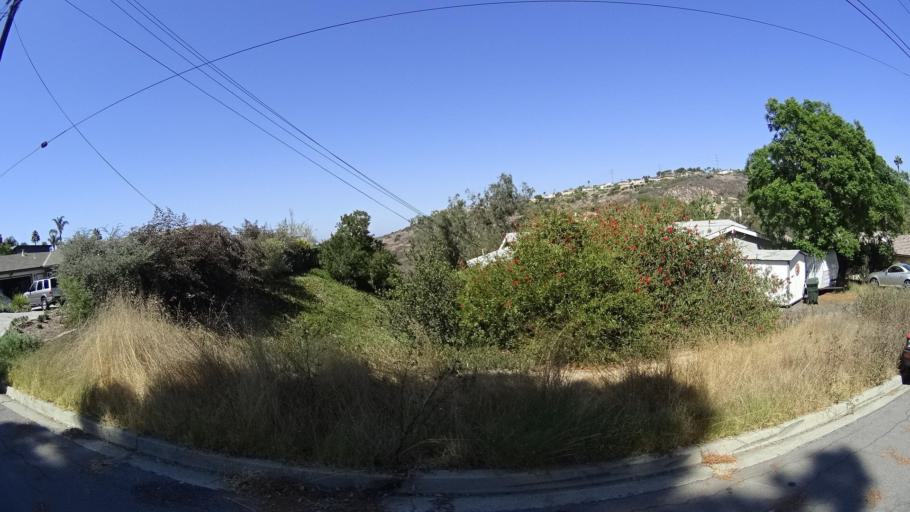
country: US
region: California
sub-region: San Diego County
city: Lake San Marcos
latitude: 33.1164
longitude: -117.2285
